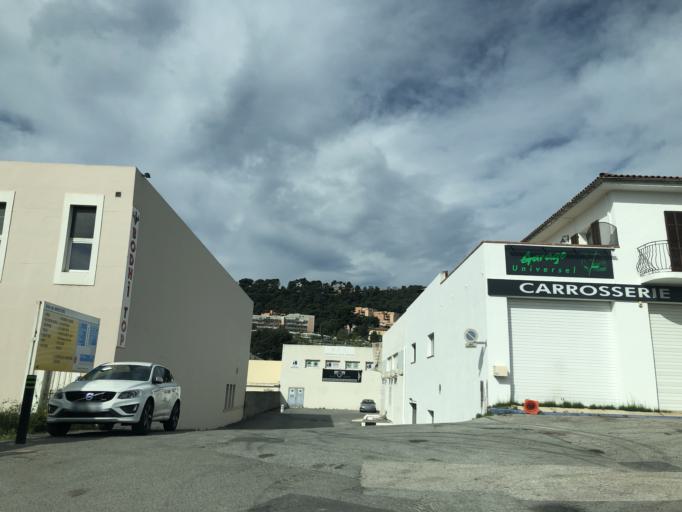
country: FR
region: Provence-Alpes-Cote d'Azur
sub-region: Departement des Alpes-Maritimes
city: Saint-Laurent-du-Var
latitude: 43.6860
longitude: 7.1875
